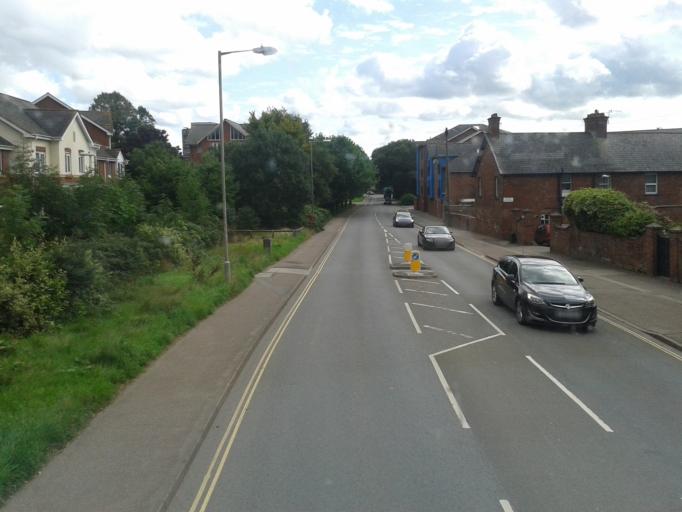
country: GB
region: England
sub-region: Devon
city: Exeter
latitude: 50.7221
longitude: -3.5389
